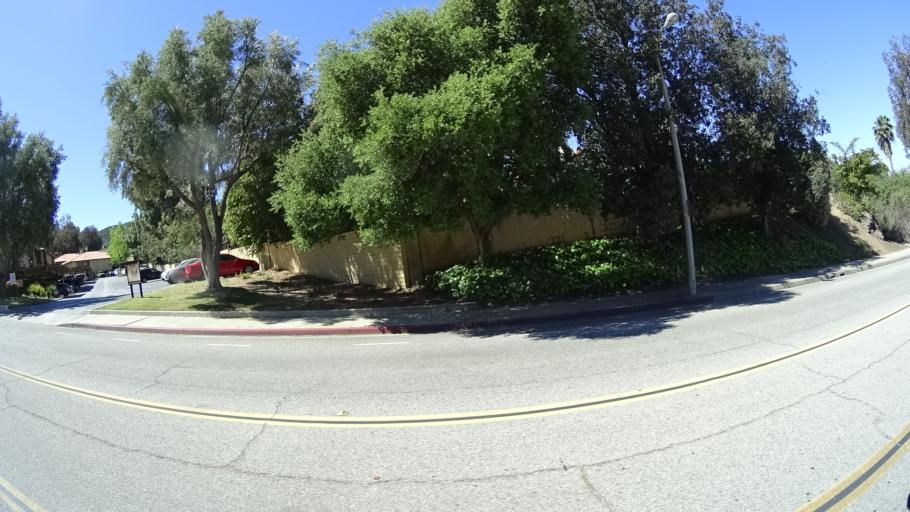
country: US
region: California
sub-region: Ventura County
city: Thousand Oaks
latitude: 34.1748
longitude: -118.8724
